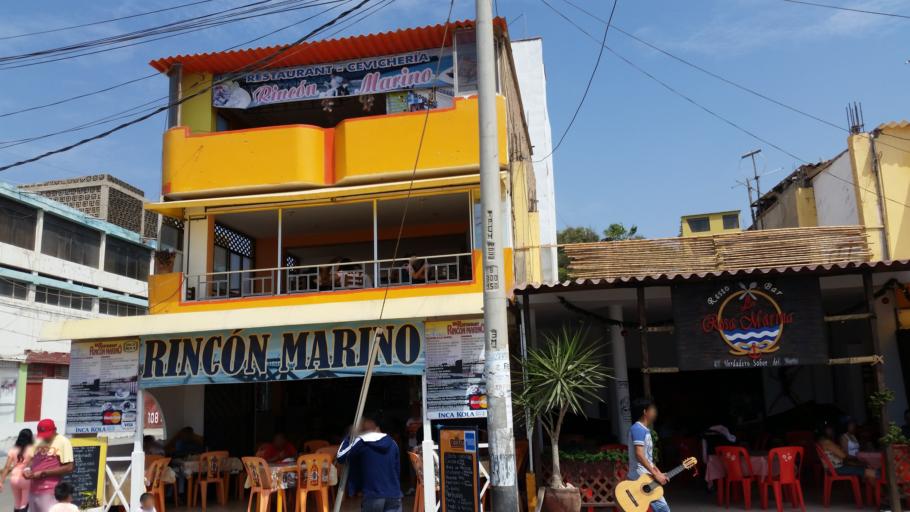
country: PE
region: Lambayeque
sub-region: Provincia de Chiclayo
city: Pimentel
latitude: -6.8411
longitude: -79.9374
